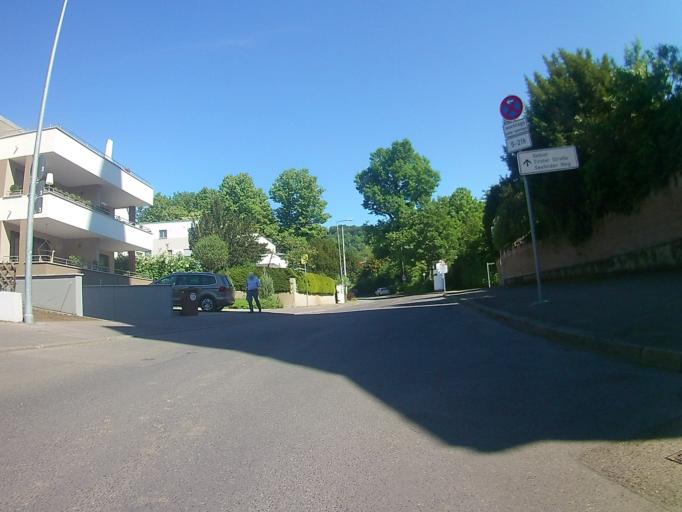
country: DE
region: Baden-Wuerttemberg
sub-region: Regierungsbezirk Stuttgart
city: Fellbach
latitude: 48.7759
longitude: 9.2798
